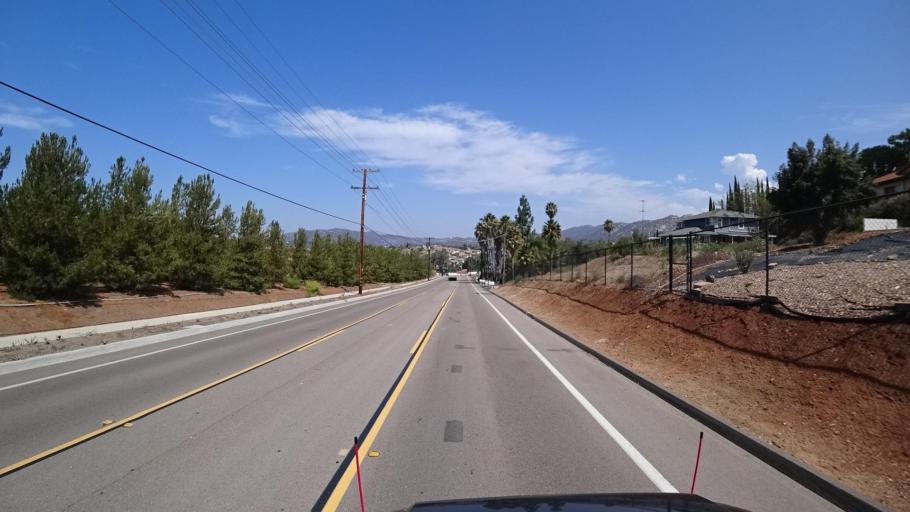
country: US
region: California
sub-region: San Diego County
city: Escondido
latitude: 33.1525
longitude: -117.0830
